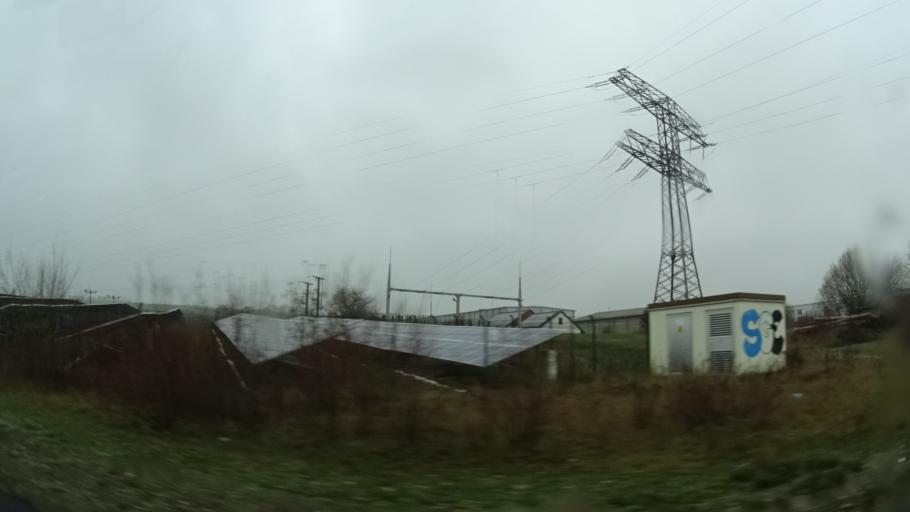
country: DE
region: Thuringia
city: Eisfeld
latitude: 50.4393
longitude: 10.9092
